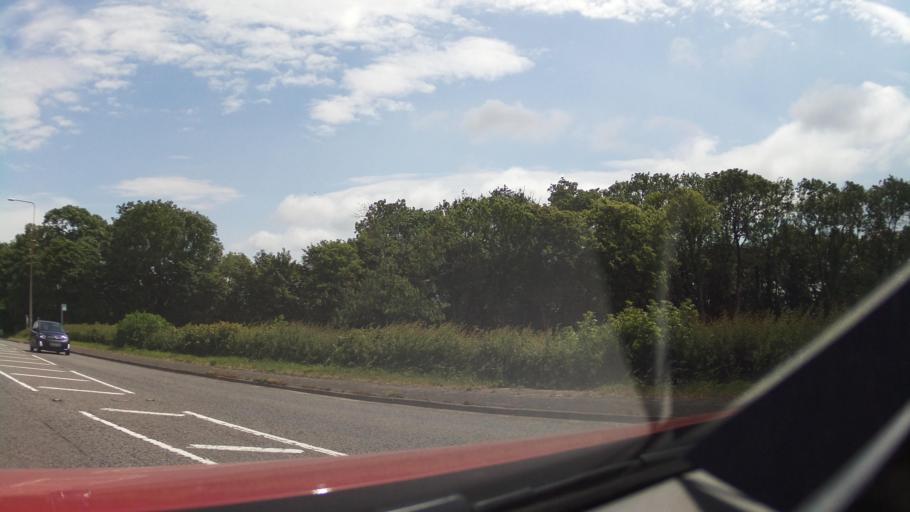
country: GB
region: Wales
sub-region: Vale of Glamorgan
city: Llangan
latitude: 51.4753
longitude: -3.5068
